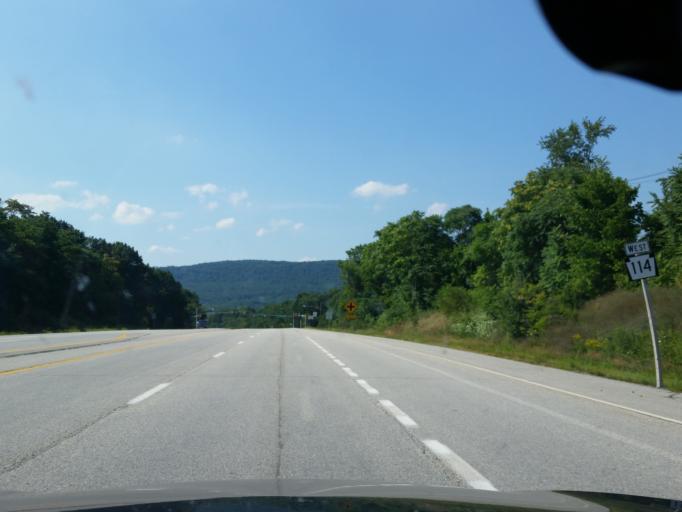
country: US
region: Pennsylvania
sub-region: Cumberland County
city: Mechanicsburg
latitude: 40.2710
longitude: -77.0447
